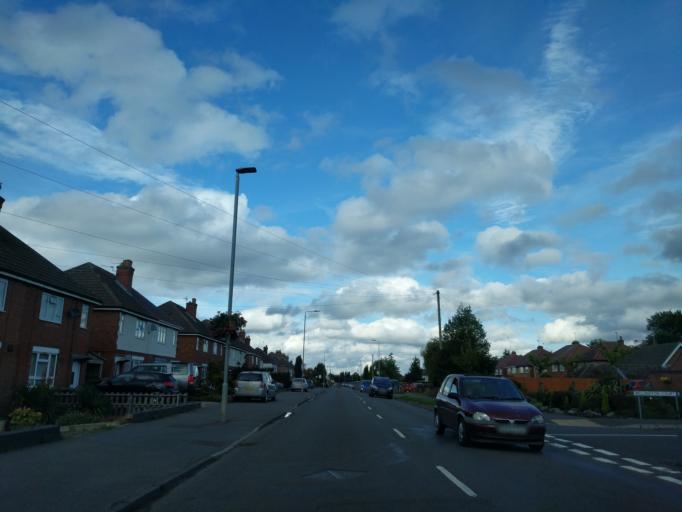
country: GB
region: England
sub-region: Leicestershire
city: Ibstock
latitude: 52.6951
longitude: -1.3960
